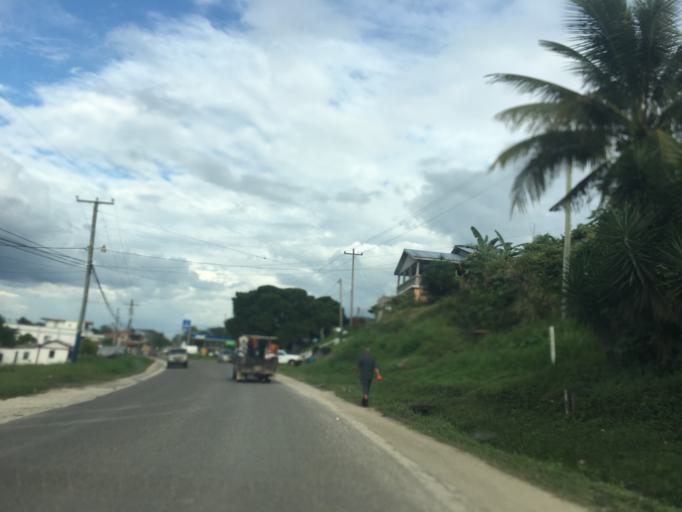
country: BZ
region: Cayo
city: San Ignacio
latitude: 17.1491
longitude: -89.0770
